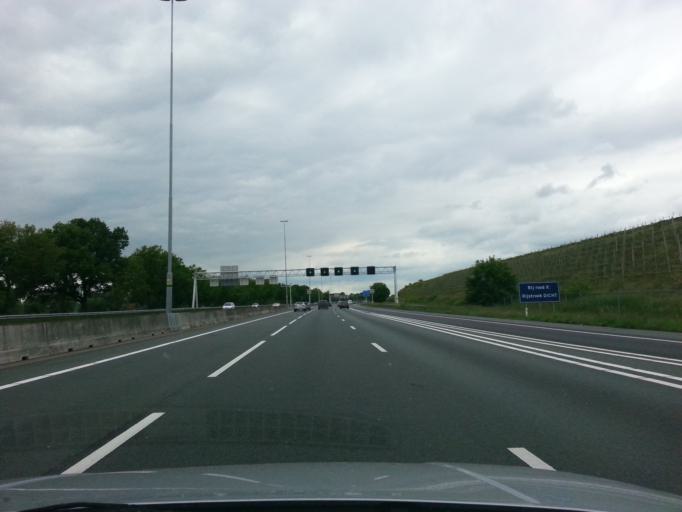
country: NL
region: Gelderland
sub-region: Gemeente Ede
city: Ede
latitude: 52.0153
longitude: 5.6476
